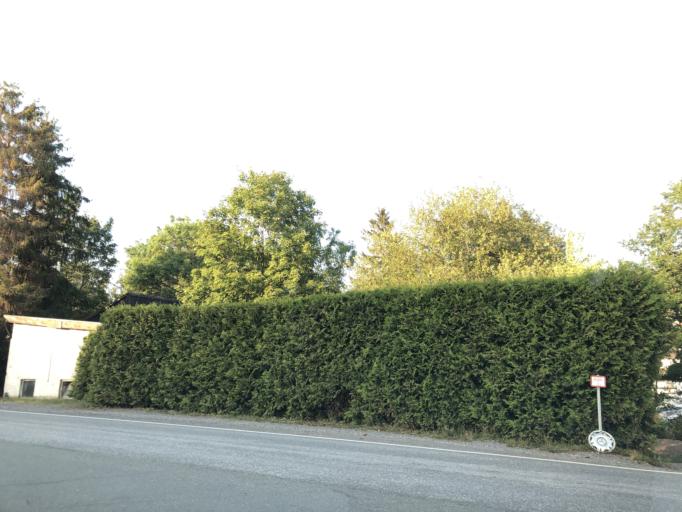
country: DE
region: North Rhine-Westphalia
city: Hallenberg
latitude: 51.1166
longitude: 8.6179
